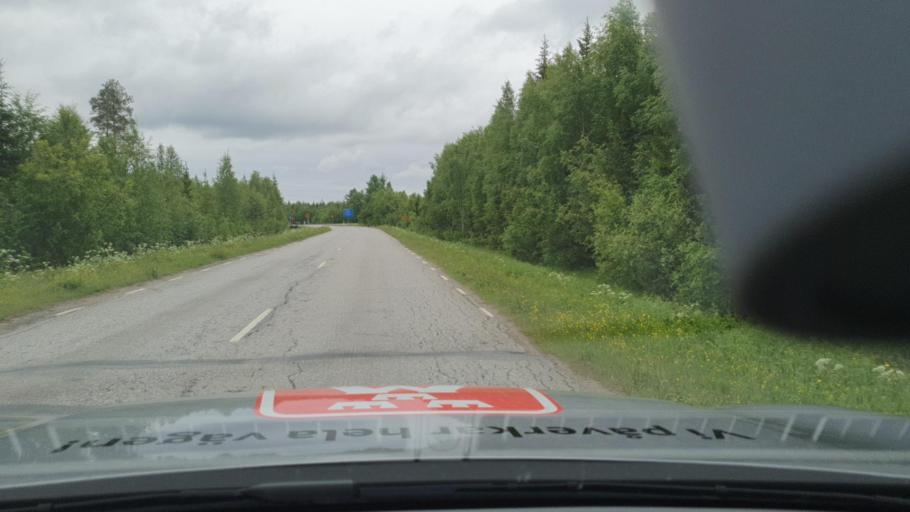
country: SE
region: Norrbotten
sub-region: Lulea Kommun
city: Ranea
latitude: 65.8437
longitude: 22.2579
